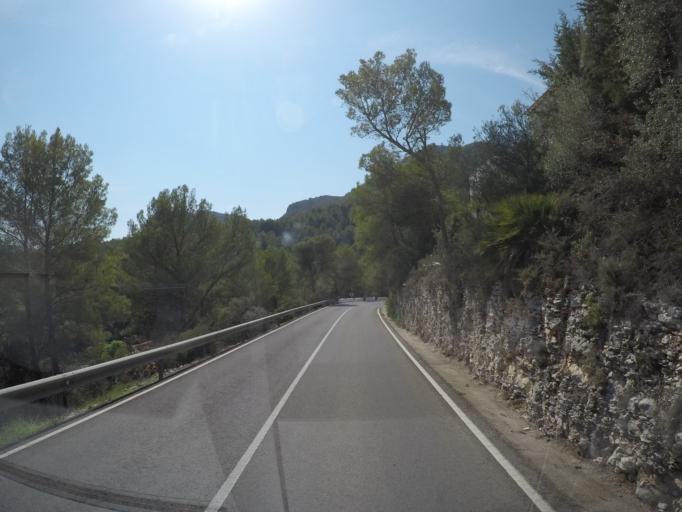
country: ES
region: Valencia
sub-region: Provincia de Alicante
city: Orba
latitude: 38.7811
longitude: -0.0791
